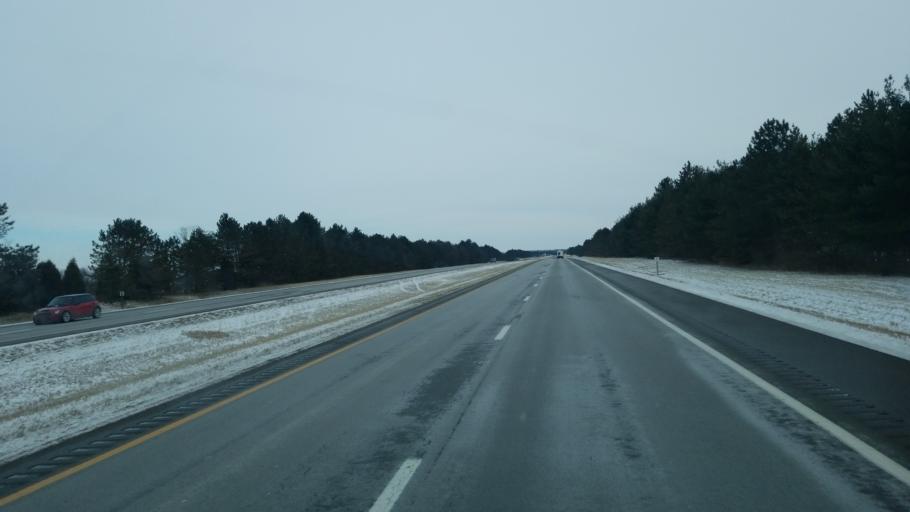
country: US
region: Ohio
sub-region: Wyandot County
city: Carey
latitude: 40.9550
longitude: -83.4407
